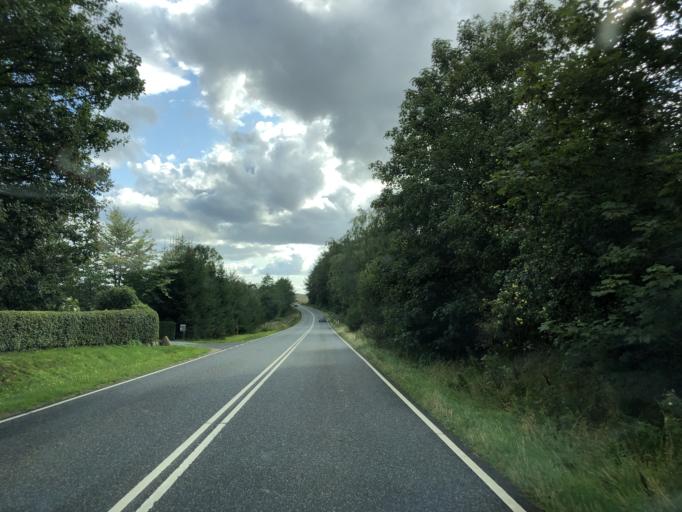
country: DK
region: Central Jutland
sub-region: Favrskov Kommune
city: Hammel
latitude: 56.2797
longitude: 9.9220
